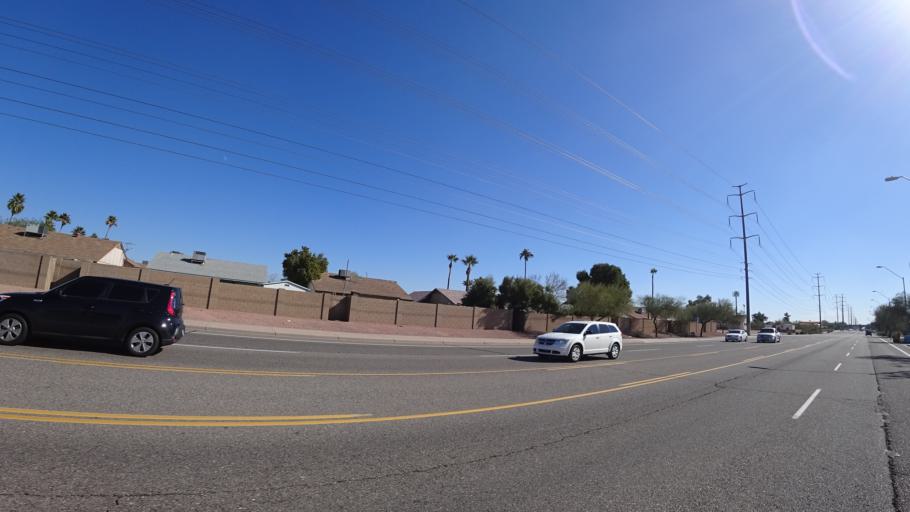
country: US
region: Arizona
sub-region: Maricopa County
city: Peoria
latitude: 33.6757
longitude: -112.1348
